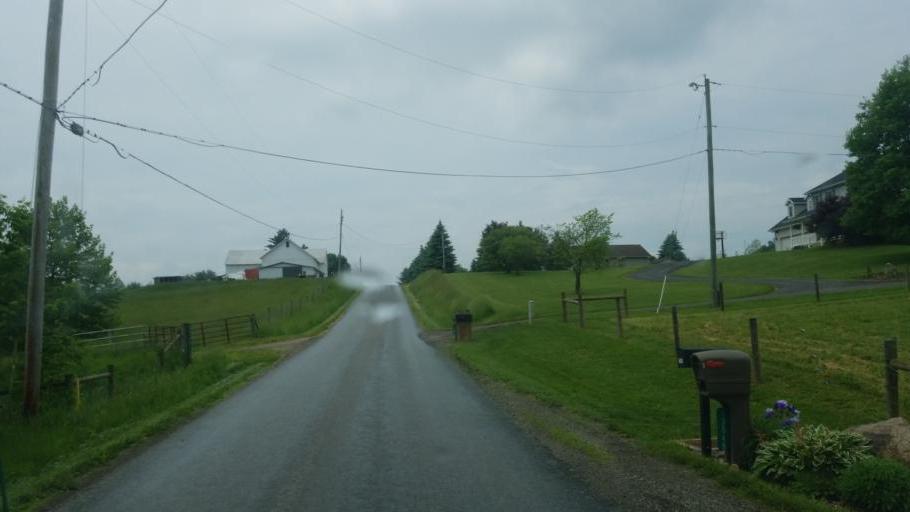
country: US
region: Ohio
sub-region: Wayne County
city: Dalton
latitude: 40.7839
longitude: -81.7395
